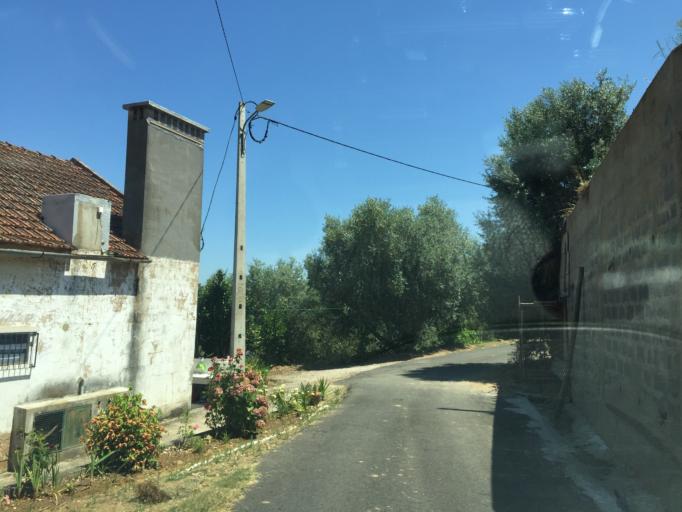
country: PT
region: Santarem
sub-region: Ferreira do Zezere
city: Ferreira do Zezere
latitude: 39.6008
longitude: -8.2747
